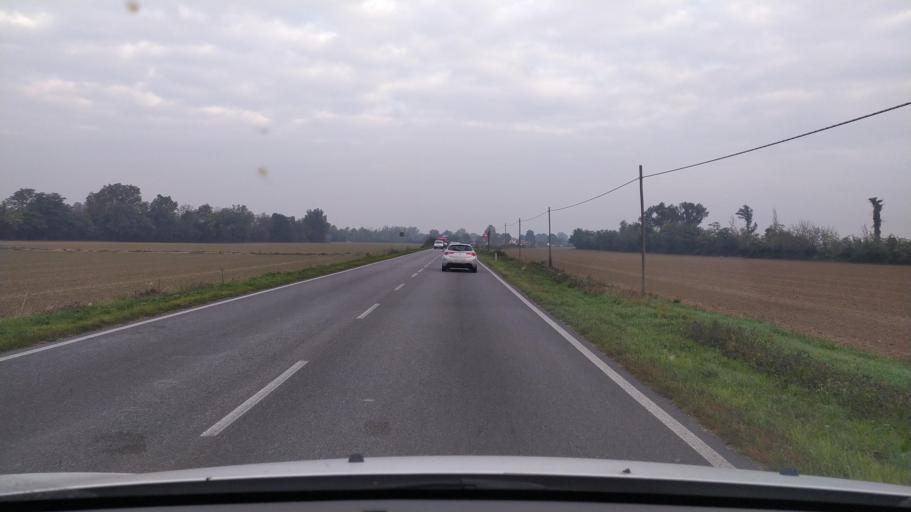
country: IT
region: Lombardy
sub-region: Citta metropolitana di Milano
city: Cisliano
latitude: 45.4442
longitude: 8.9715
